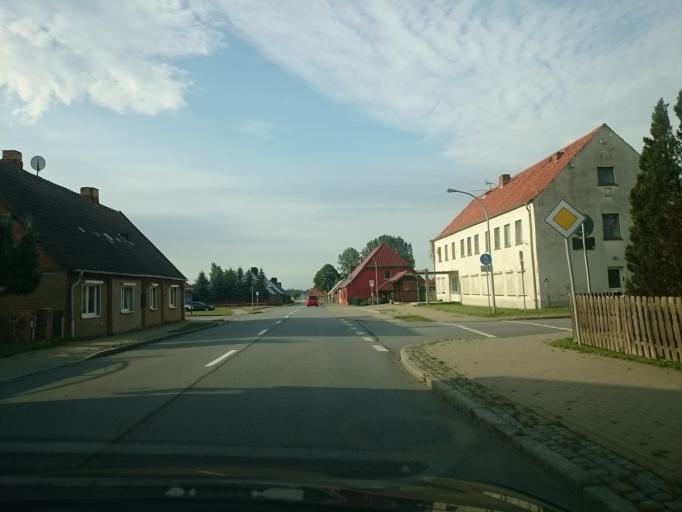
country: DE
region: Mecklenburg-Vorpommern
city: Wackerow
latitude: 53.7248
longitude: 12.9187
